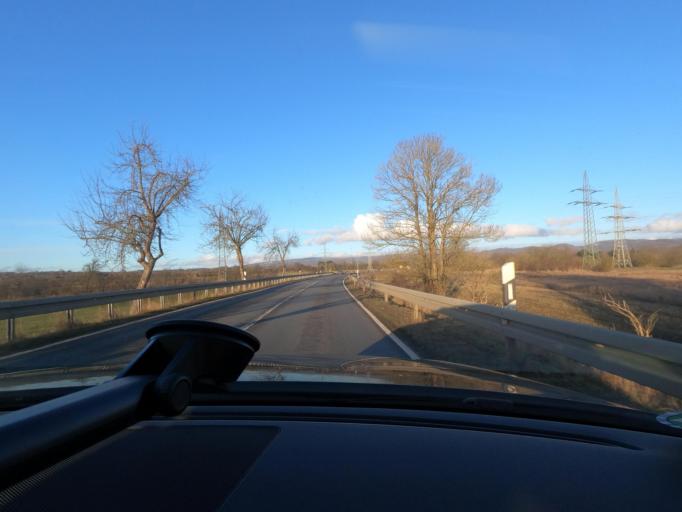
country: DE
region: Lower Saxony
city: Herzberg am Harz
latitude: 51.6221
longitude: 10.3221
